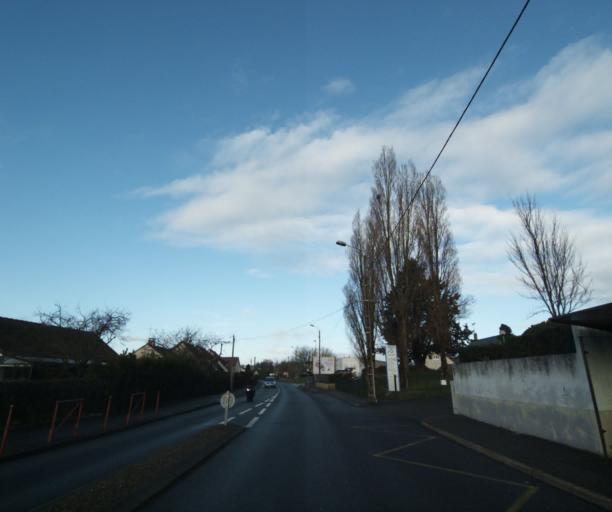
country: FR
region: Pays de la Loire
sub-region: Departement de la Sarthe
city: Coulaines
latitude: 48.0221
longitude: 0.1784
